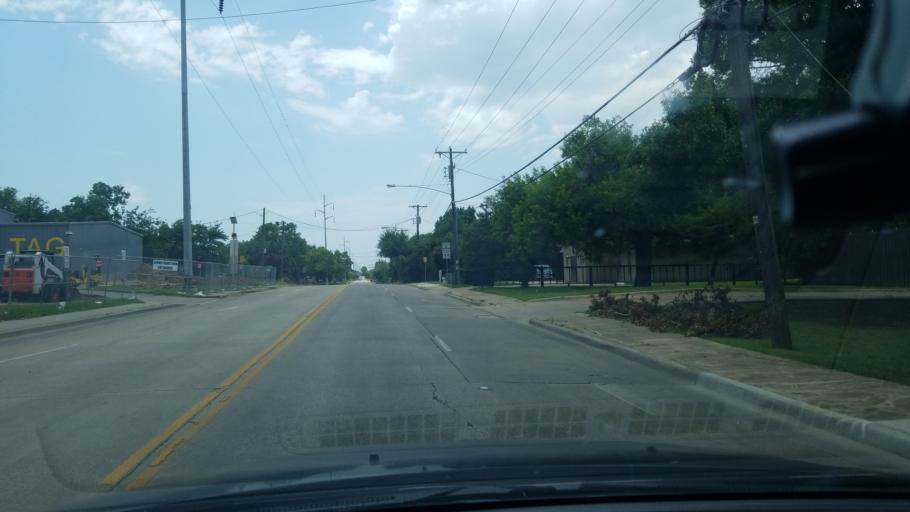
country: US
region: Texas
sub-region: Dallas County
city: Balch Springs
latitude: 32.7482
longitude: -96.6569
